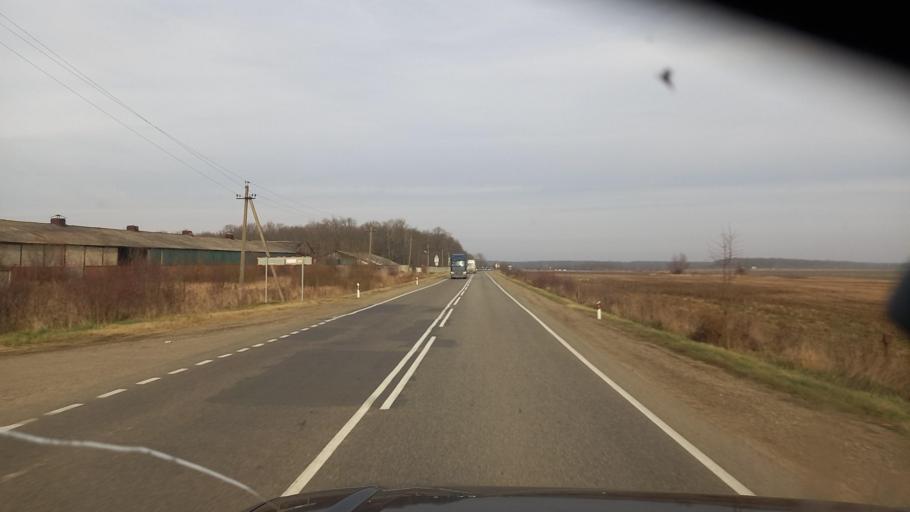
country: RU
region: Krasnodarskiy
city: Saratovskaya
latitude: 44.6873
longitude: 39.3176
